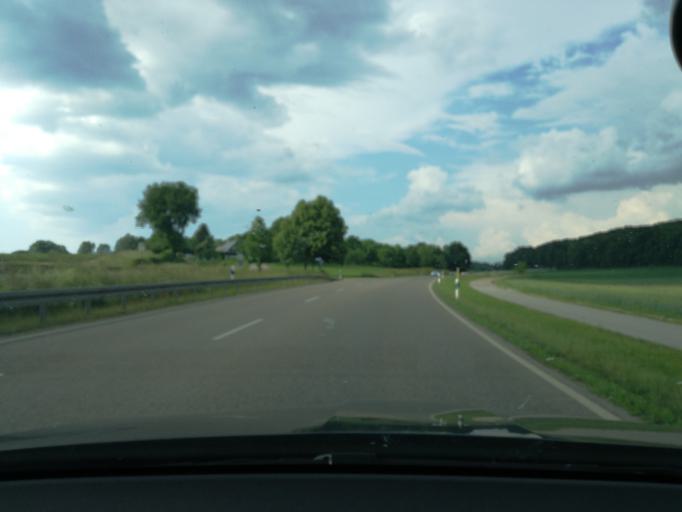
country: DE
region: Bavaria
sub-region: Upper Bavaria
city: Schondorf am Ammersee
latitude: 48.0608
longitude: 11.0892
